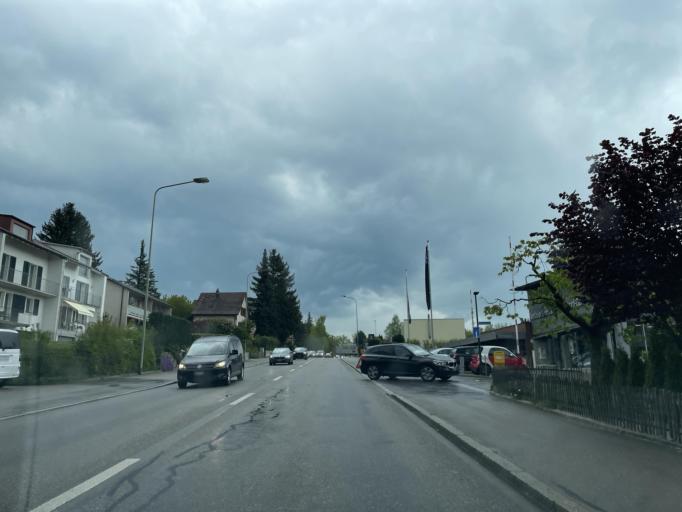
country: CH
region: Zurich
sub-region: Bezirk Winterthur
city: Veltheim
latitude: 47.5260
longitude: 8.7140
